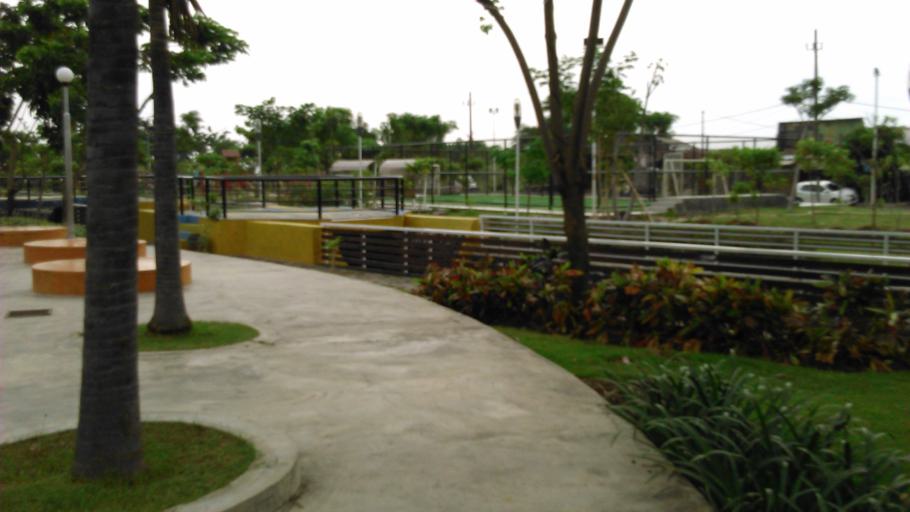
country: ID
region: East Java
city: Labansari
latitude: -7.2264
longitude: 112.7866
